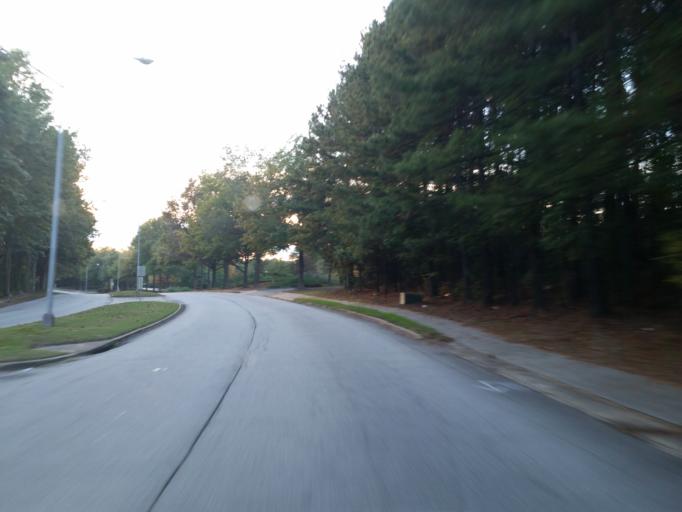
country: US
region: Georgia
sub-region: Cobb County
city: Vinings
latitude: 33.8284
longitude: -84.5017
